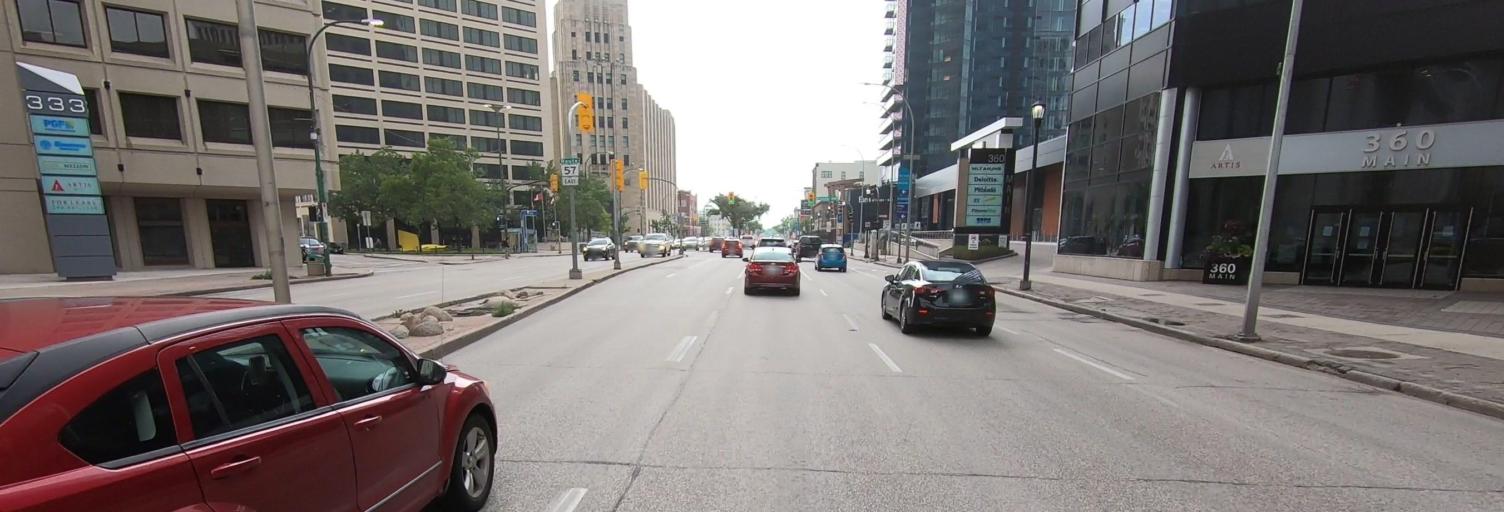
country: CA
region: Manitoba
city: Winnipeg
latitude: 49.8950
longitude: -97.1383
